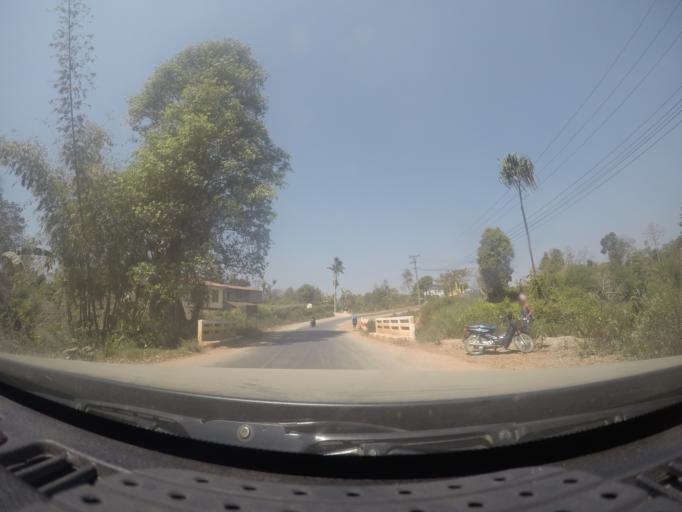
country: MM
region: Shan
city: Taunggyi
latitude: 20.9284
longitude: 96.5474
